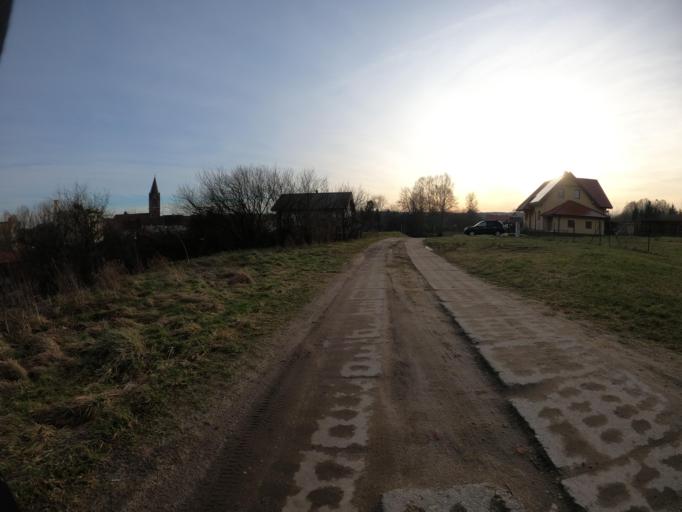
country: PL
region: West Pomeranian Voivodeship
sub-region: Powiat koszalinski
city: Polanow
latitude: 54.1205
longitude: 16.6830
